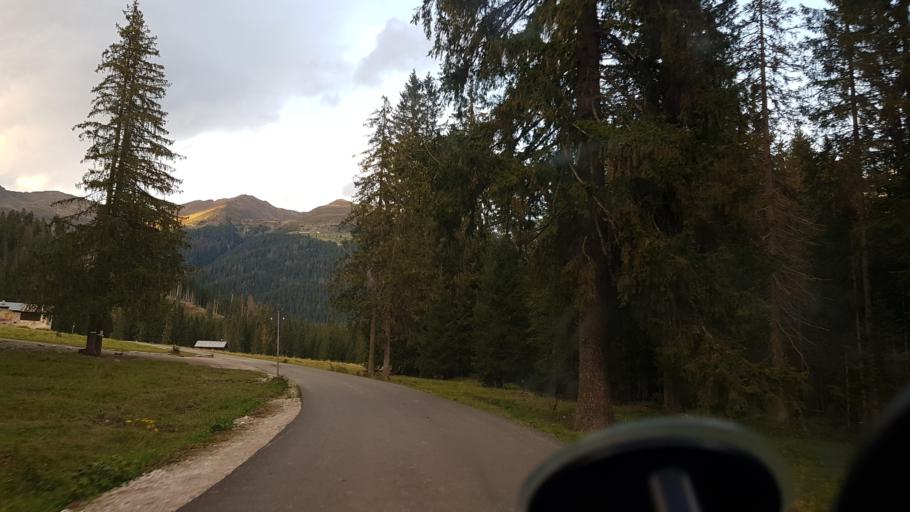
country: IT
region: Veneto
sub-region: Provincia di Belluno
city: San Pietro di Cadore
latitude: 46.6123
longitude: 12.6240
